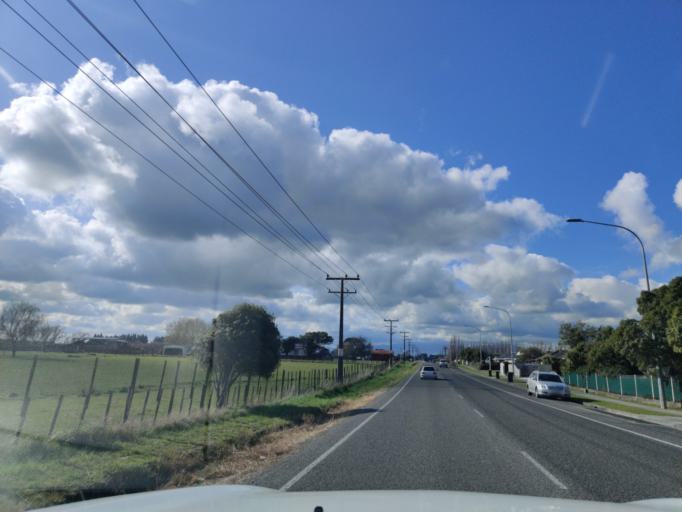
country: NZ
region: Manawatu-Wanganui
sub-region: Palmerston North City
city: Palmerston North
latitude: -40.3200
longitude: 175.6536
